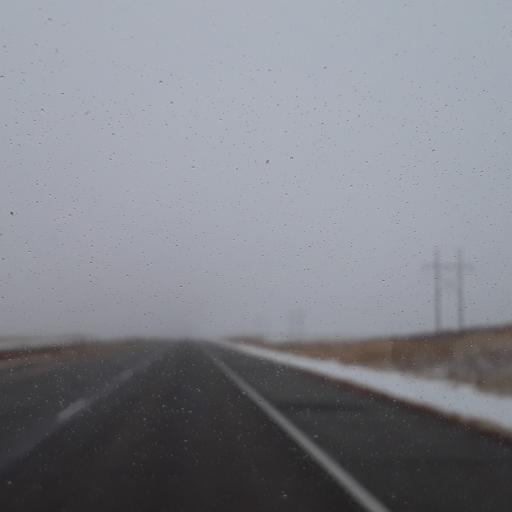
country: US
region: Nebraska
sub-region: Cheyenne County
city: Sidney
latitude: 40.7996
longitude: -102.8694
